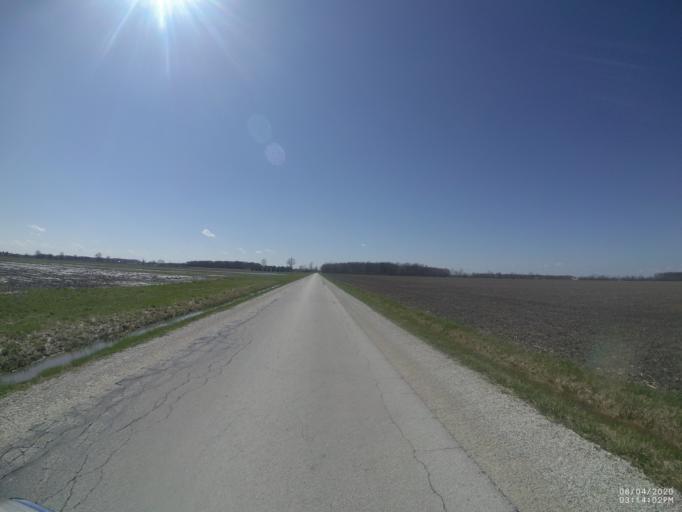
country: US
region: Ohio
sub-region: Sandusky County
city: Ballville
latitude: 41.2834
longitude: -83.1982
